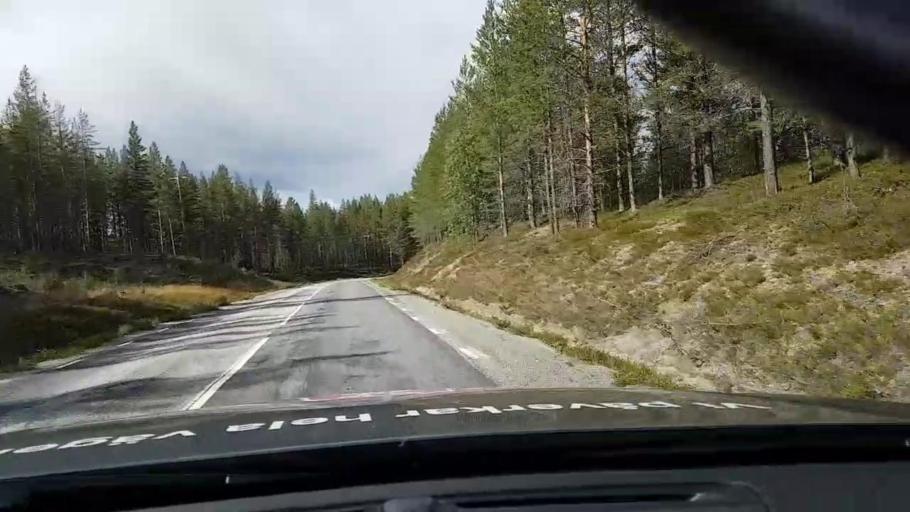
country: SE
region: Vaesterbotten
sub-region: Asele Kommun
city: Asele
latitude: 63.8560
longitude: 17.3867
